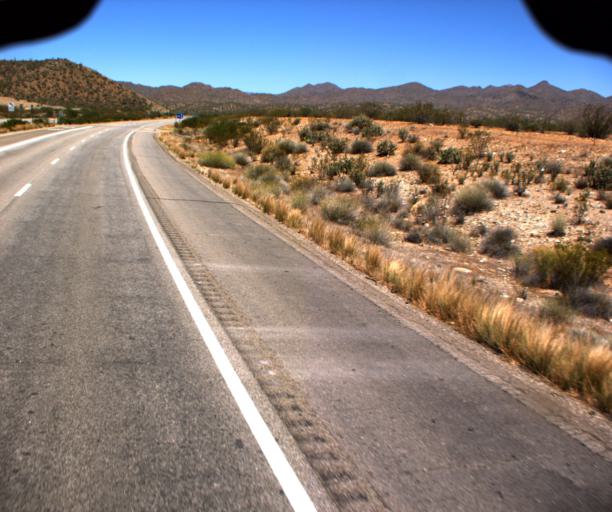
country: US
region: Arizona
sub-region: Yavapai County
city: Bagdad
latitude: 34.3713
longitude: -113.1879
